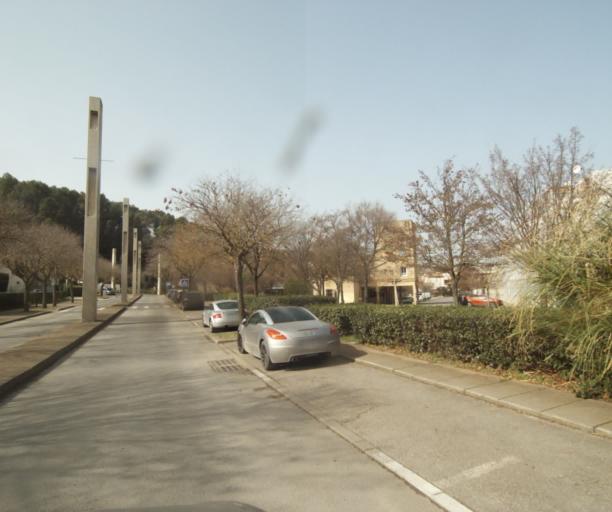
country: FR
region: Provence-Alpes-Cote d'Azur
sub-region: Departement des Bouches-du-Rhone
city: Gardanne
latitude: 43.4515
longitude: 5.4703
